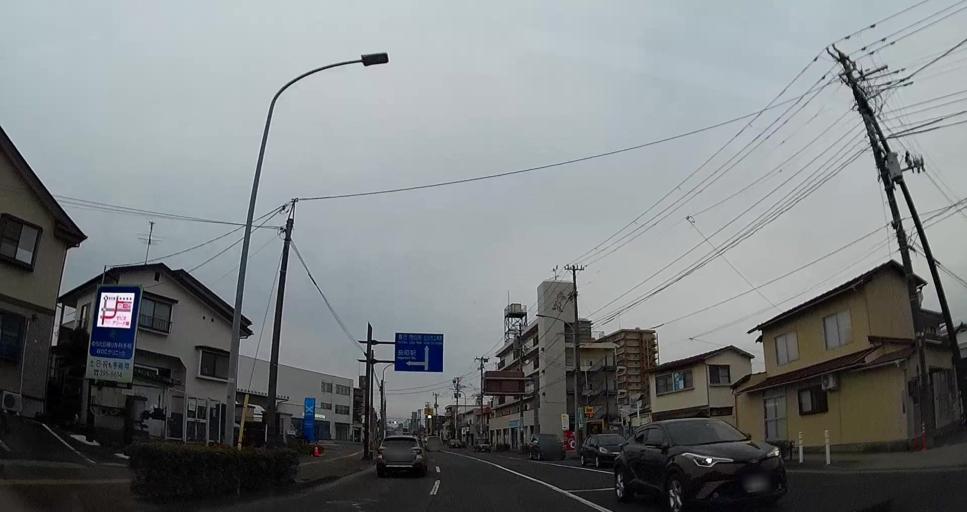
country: JP
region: Miyagi
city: Sendai
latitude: 38.2253
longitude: 140.8968
